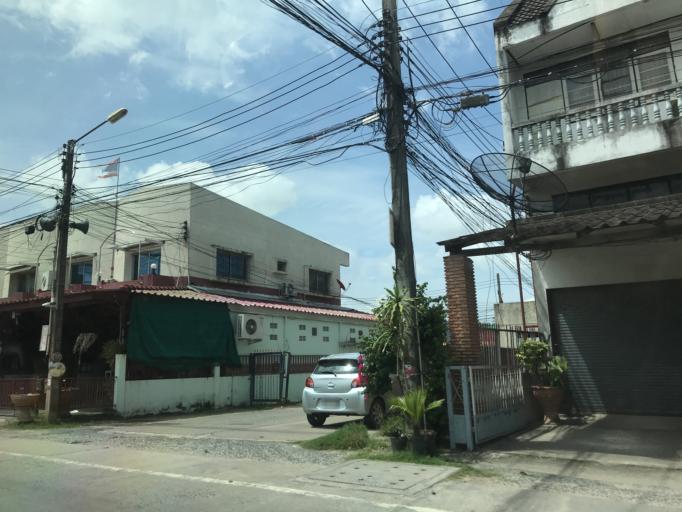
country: TH
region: Chon Buri
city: Si Racha
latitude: 13.1468
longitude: 100.9521
